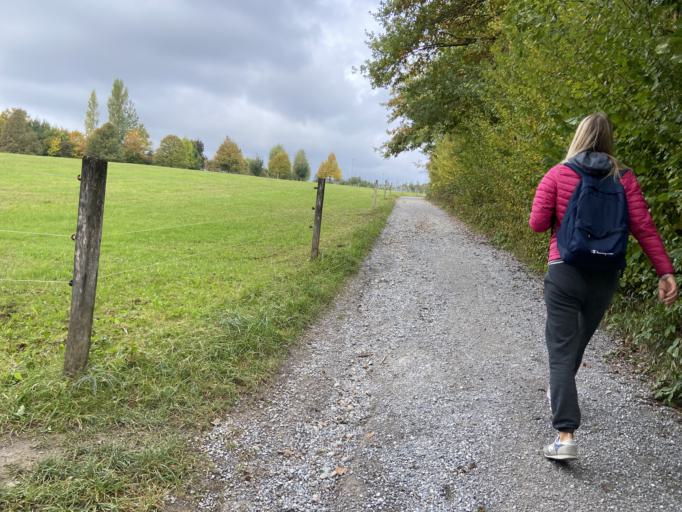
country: CH
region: Zurich
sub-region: Bezirk Meilen
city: Maennedorf / Ausserfeld
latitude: 47.2560
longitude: 8.7149
